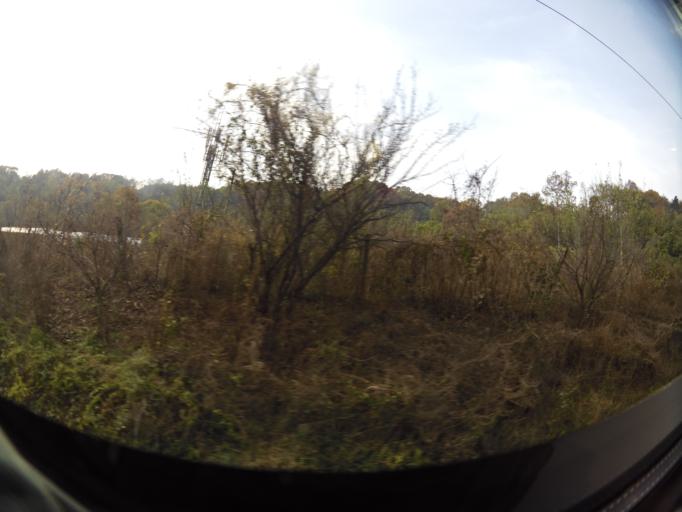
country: KR
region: Gyeongsangbuk-do
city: Gimcheon
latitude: 36.1368
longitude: 128.0161
